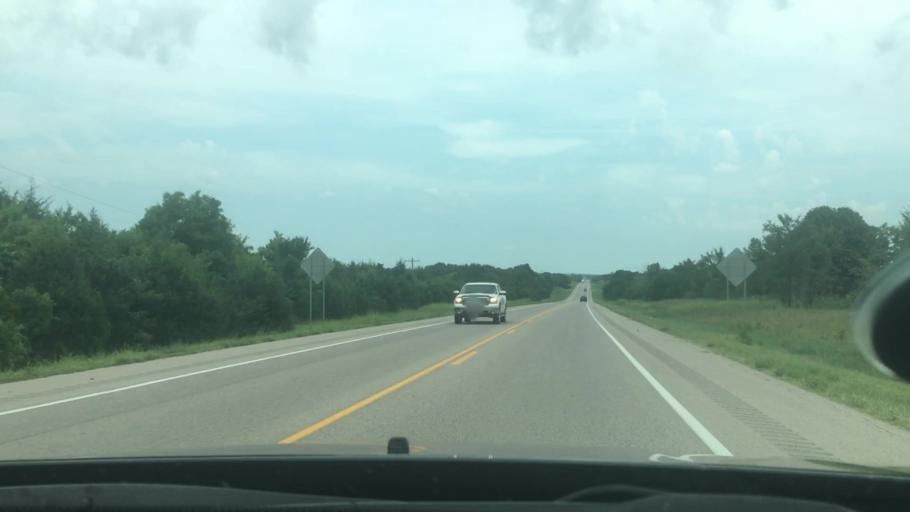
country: US
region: Oklahoma
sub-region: Seminole County
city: Konawa
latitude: 34.9866
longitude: -96.6793
